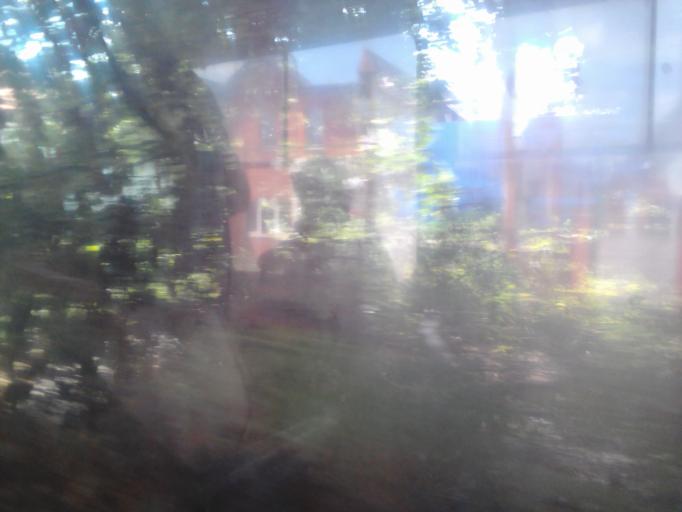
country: RU
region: Kursk
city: Kursk
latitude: 51.7450
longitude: 36.1682
